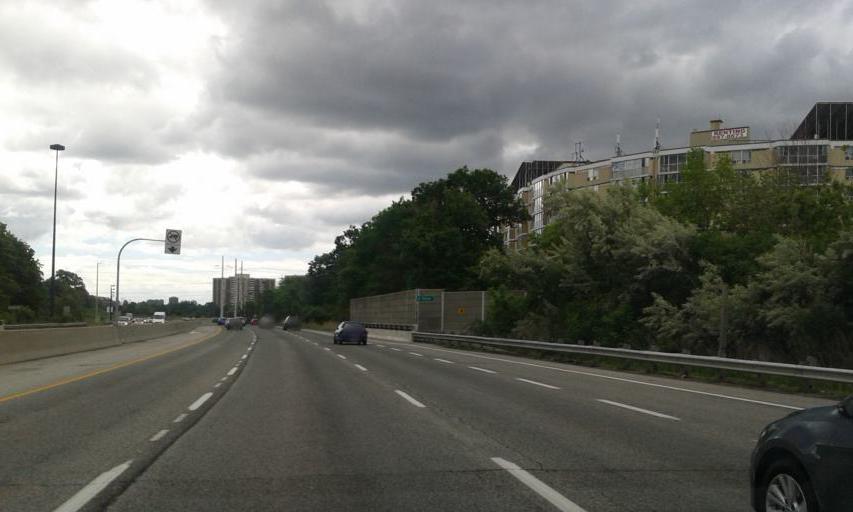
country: CA
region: Ontario
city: Willowdale
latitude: 43.7200
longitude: -79.3291
